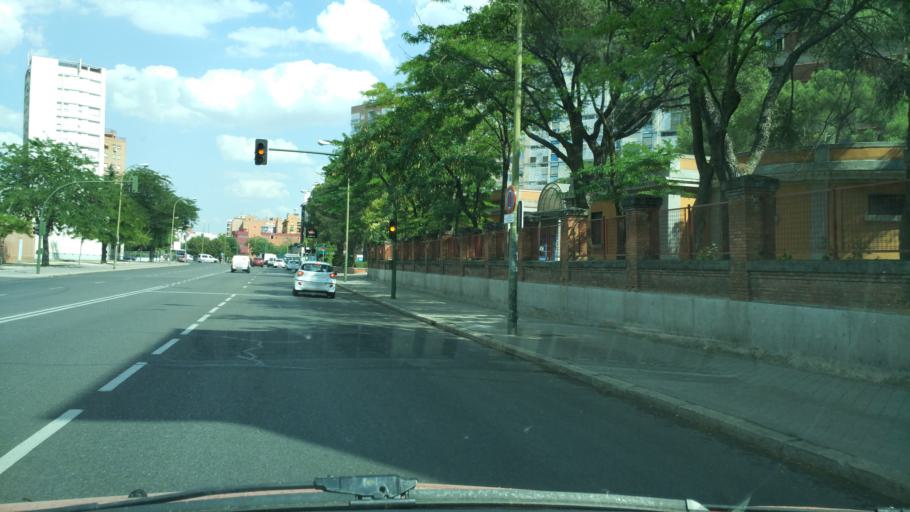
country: ES
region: Madrid
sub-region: Provincia de Madrid
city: Tetuan de las Victorias
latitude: 40.4584
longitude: -3.7151
